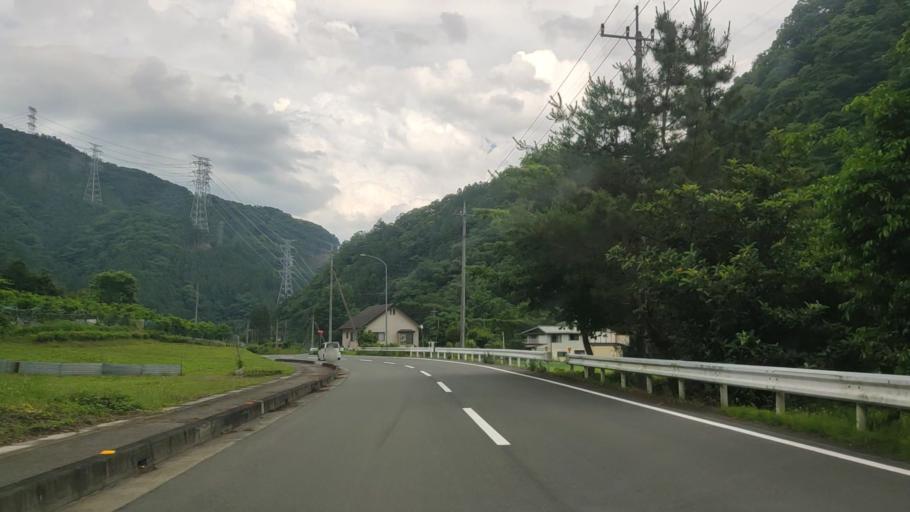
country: JP
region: Saitama
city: Chichibu
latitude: 36.0329
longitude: 138.9293
